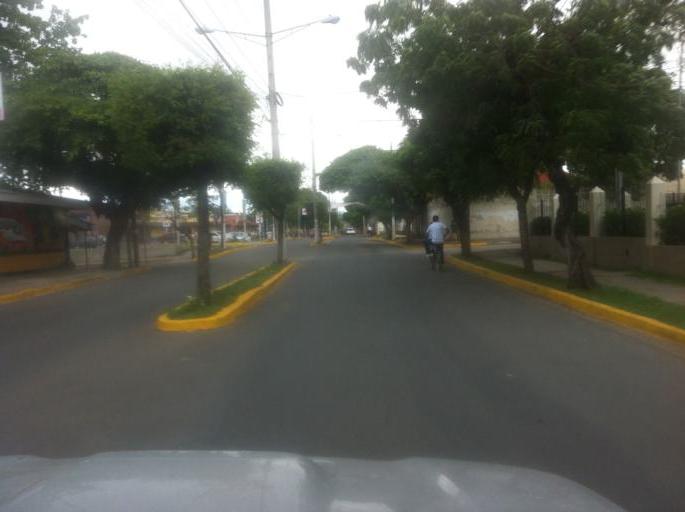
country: NI
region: Granada
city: Granada
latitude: 11.9367
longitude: -85.9576
